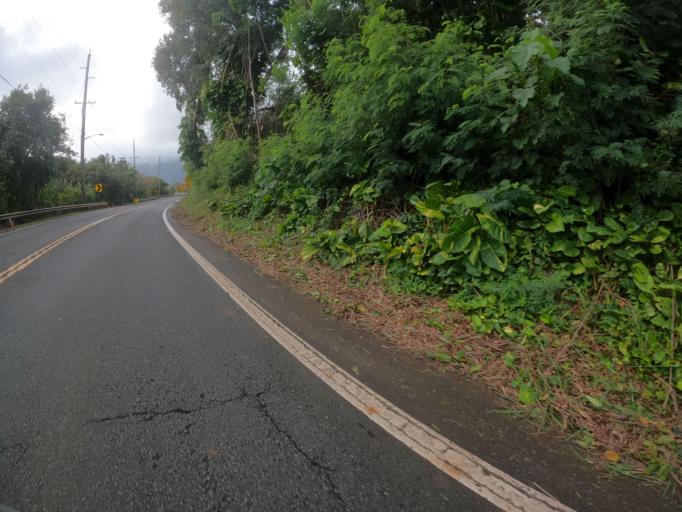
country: US
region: Hawaii
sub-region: Honolulu County
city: Kahalu'u
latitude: 21.4767
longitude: -157.8425
